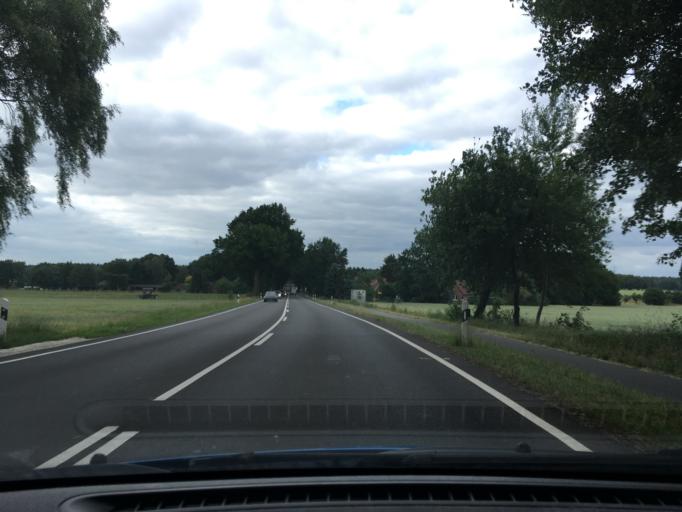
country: DE
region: Lower Saxony
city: Drestedt
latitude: 53.3294
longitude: 9.8134
